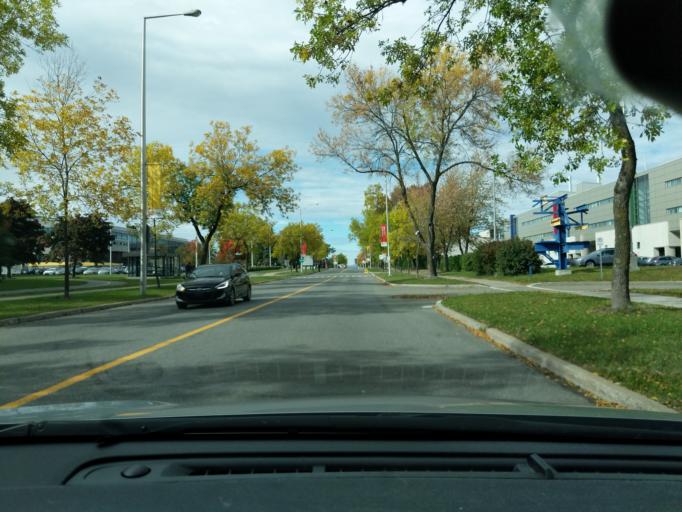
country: CA
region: Quebec
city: Quebec
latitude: 46.7774
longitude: -71.2748
